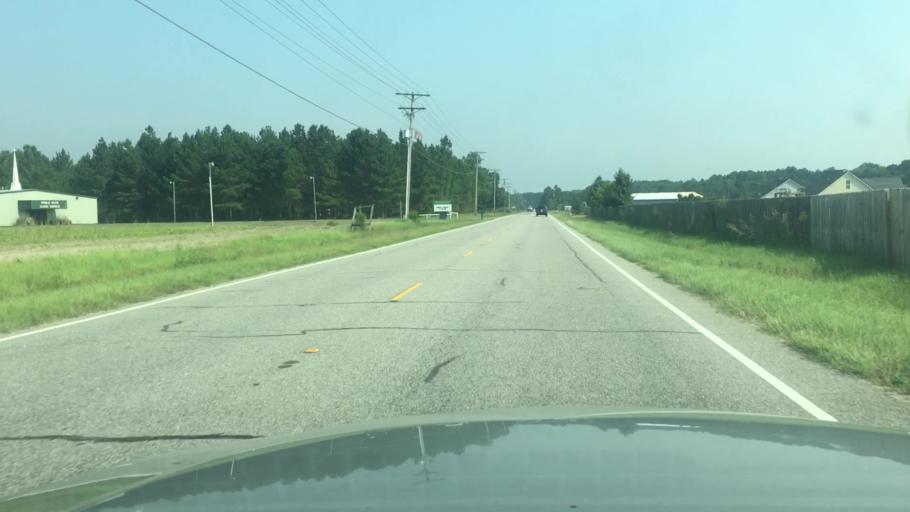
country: US
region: North Carolina
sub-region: Cumberland County
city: Hope Mills
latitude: 34.9022
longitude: -78.9014
